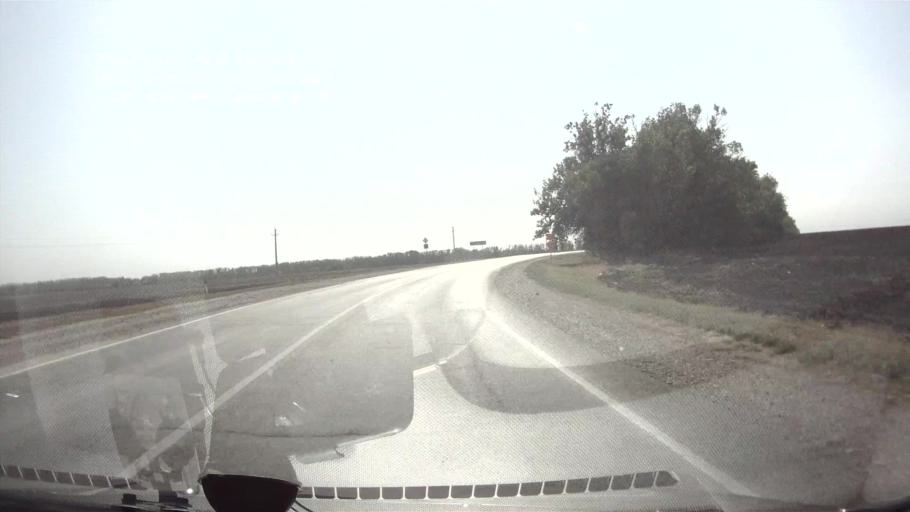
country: RU
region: Krasnodarskiy
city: Dmitriyevskaya
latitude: 45.6987
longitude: 40.7437
